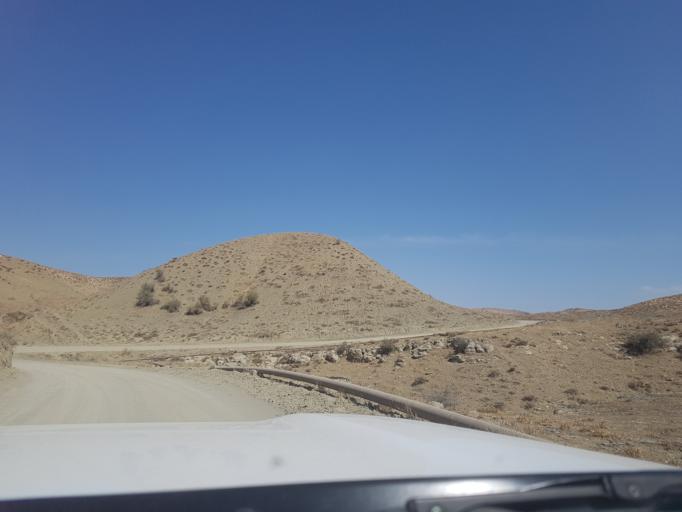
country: TM
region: Ahal
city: Baharly
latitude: 38.2446
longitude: 56.8906
